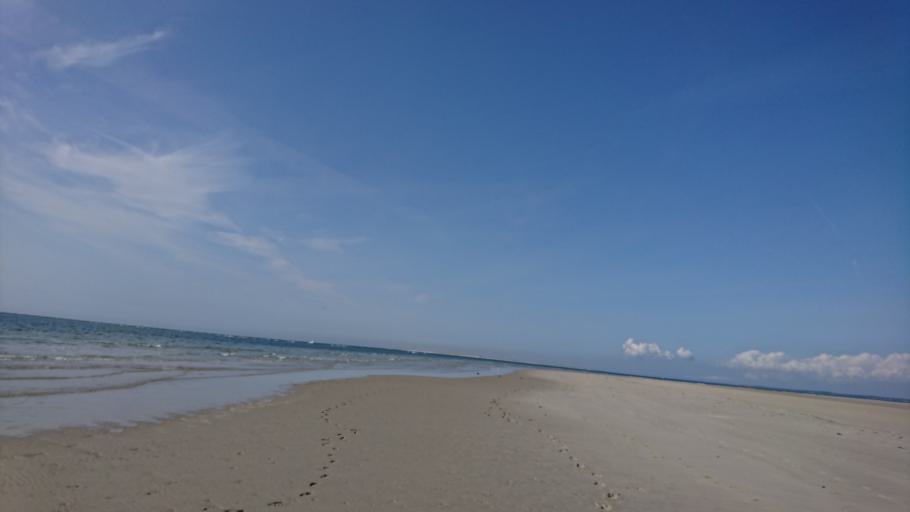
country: DK
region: South Denmark
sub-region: Fano Kommune
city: Nordby
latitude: 55.4501
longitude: 8.3272
